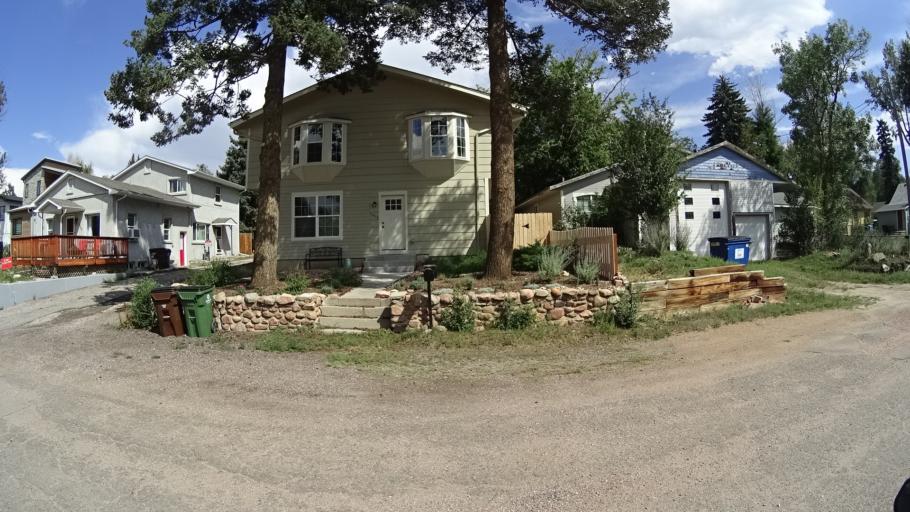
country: US
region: Colorado
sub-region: El Paso County
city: Colorado Springs
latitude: 38.8481
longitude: -104.8102
